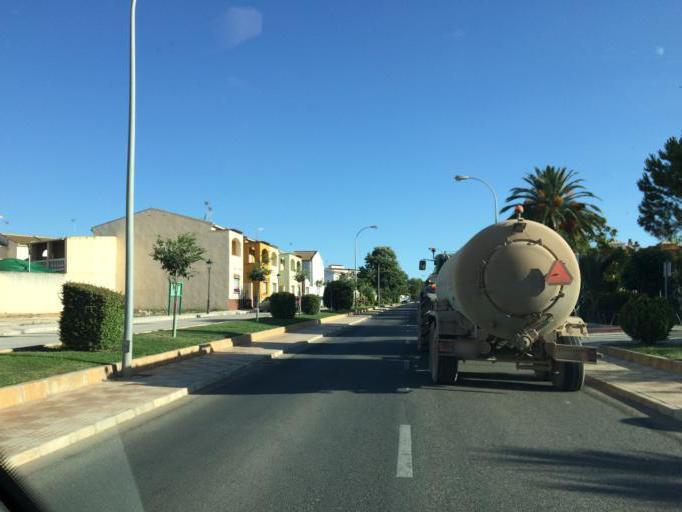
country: ES
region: Andalusia
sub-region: Provincia de Malaga
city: Campillos
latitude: 37.0422
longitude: -4.8599
